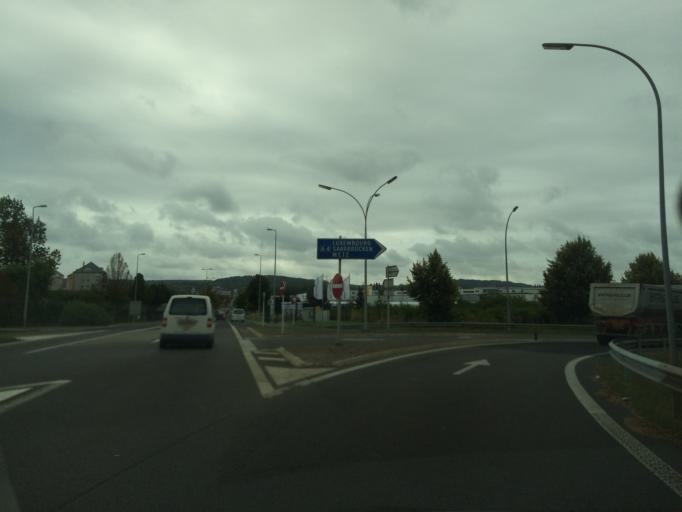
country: LU
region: Luxembourg
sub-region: Canton d'Esch-sur-Alzette
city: Esch-sur-Alzette
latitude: 49.5123
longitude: 5.9763
